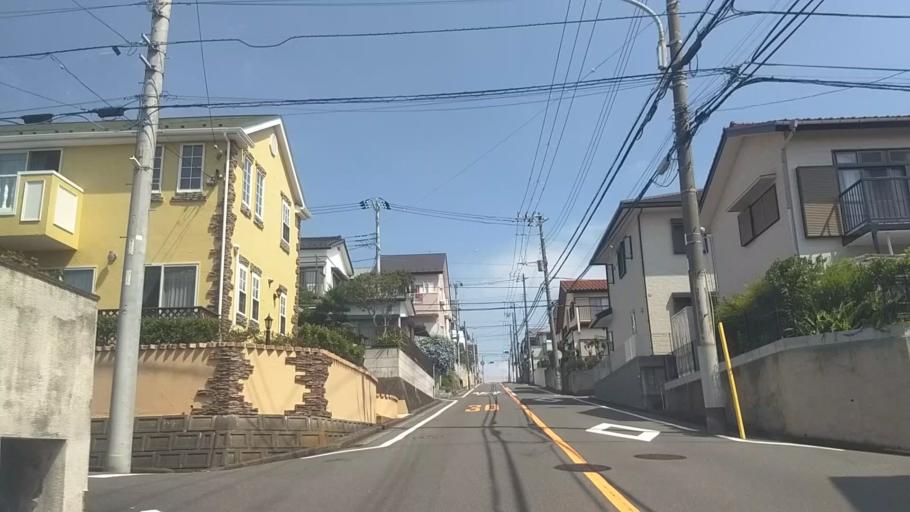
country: JP
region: Kanagawa
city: Zushi
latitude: 35.3316
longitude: 139.6037
